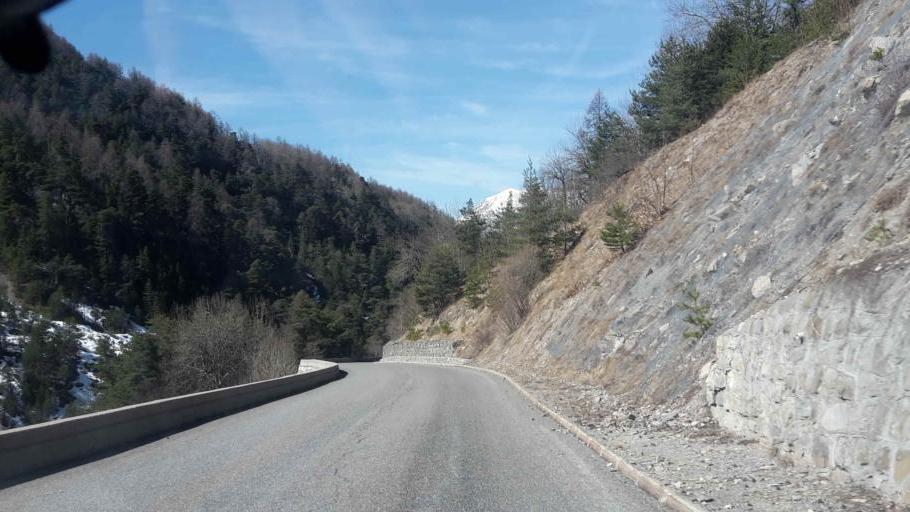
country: FR
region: Provence-Alpes-Cote d'Azur
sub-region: Departement des Hautes-Alpes
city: Embrun
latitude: 44.5508
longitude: 6.5812
